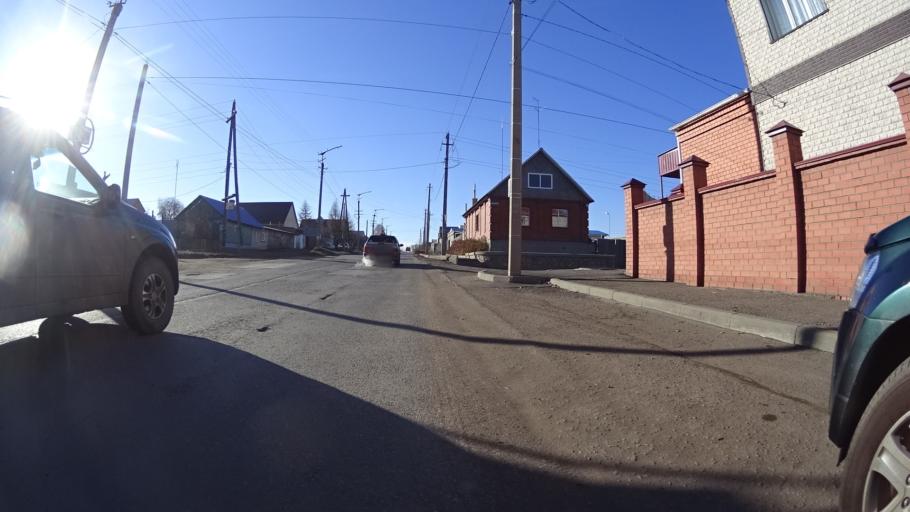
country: RU
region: Chelyabinsk
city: Troitsk
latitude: 54.0889
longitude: 61.5372
